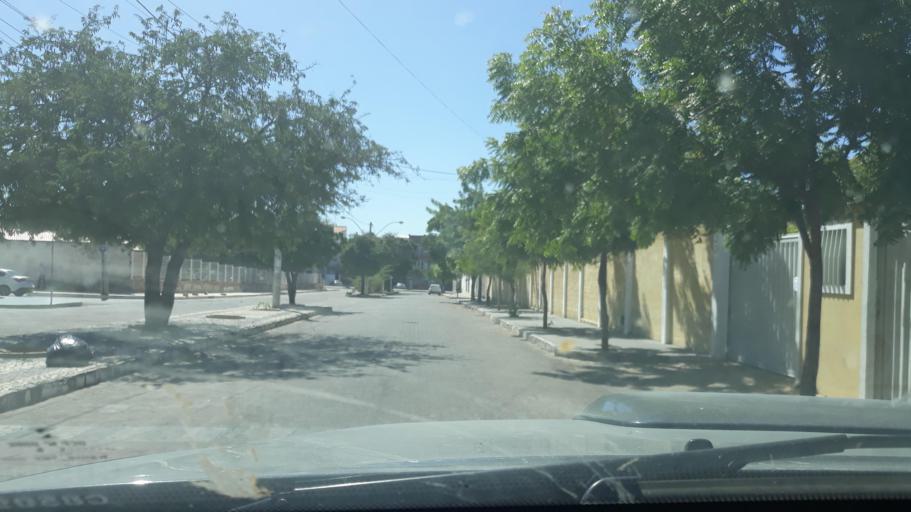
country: BR
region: Bahia
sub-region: Guanambi
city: Guanambi
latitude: -14.2183
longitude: -42.7838
